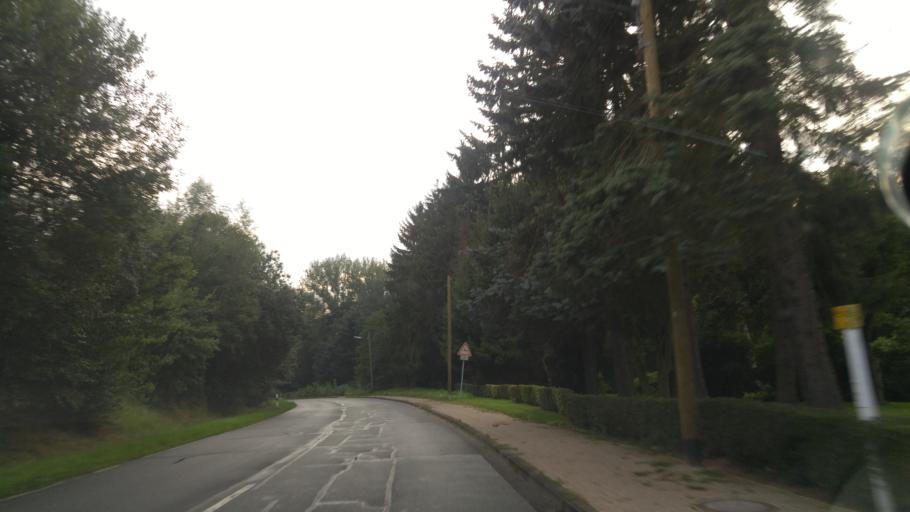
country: DE
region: North Rhine-Westphalia
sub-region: Regierungsbezirk Detmold
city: Bielefeld
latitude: 52.0792
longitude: 8.5331
